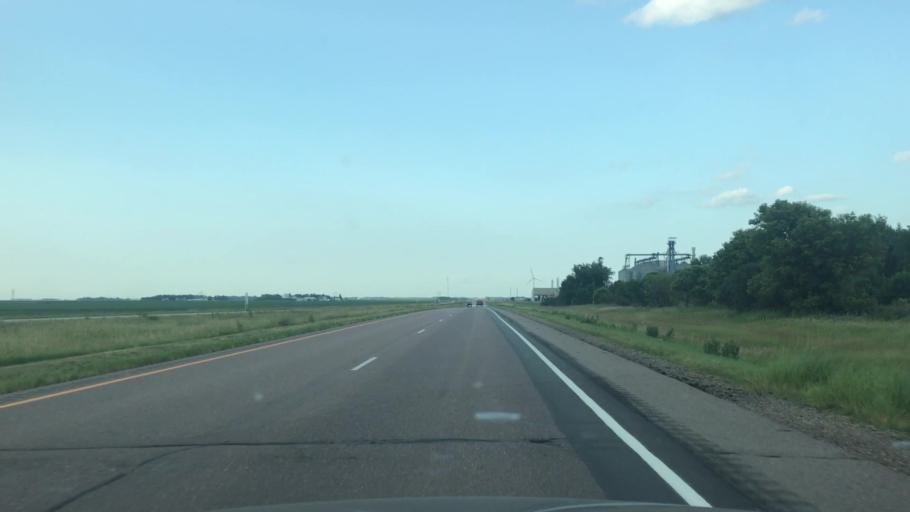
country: US
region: Minnesota
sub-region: Nobles County
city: Worthington
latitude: 43.7010
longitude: -95.4679
